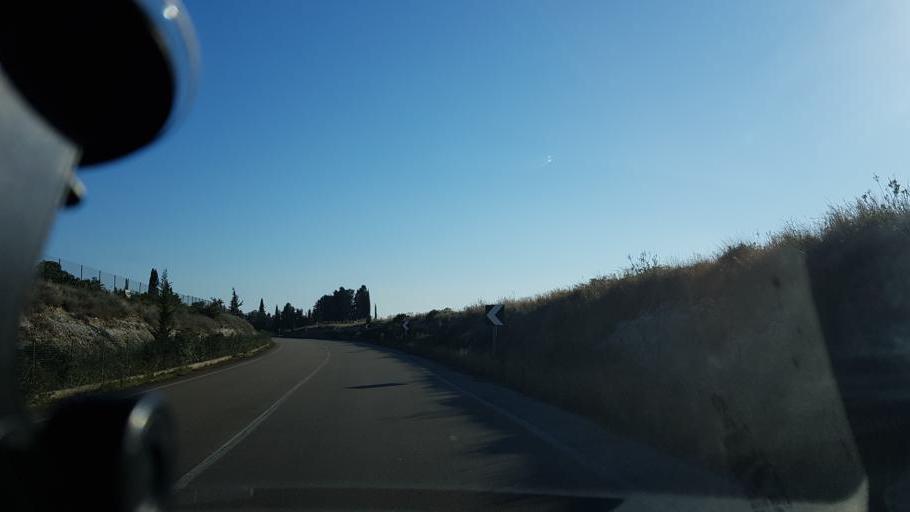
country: IT
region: Apulia
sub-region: Provincia di Lecce
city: Merine
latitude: 40.4048
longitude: 18.2502
